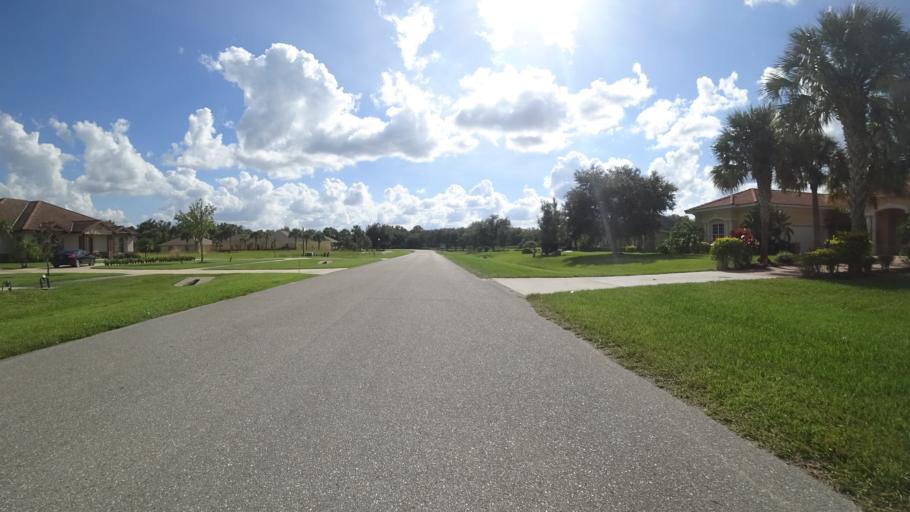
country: US
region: Florida
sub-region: Manatee County
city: Ellenton
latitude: 27.5422
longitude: -82.3929
